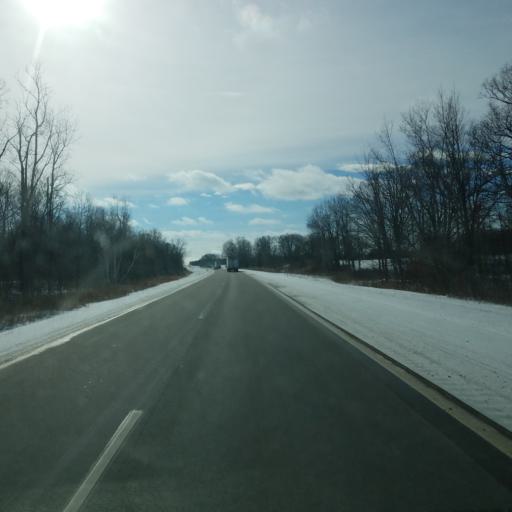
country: US
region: Michigan
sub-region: Gratiot County
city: Ithaca
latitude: 43.3323
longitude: -84.6028
